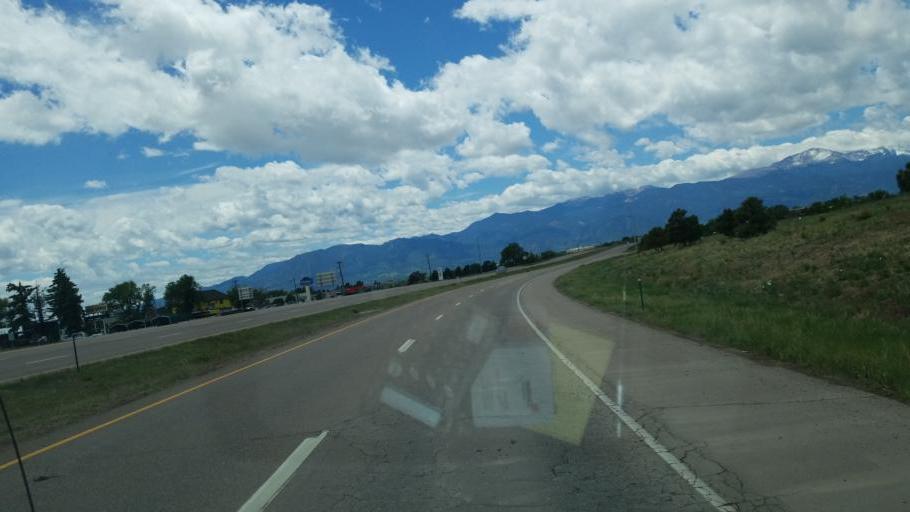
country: US
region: Colorado
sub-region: El Paso County
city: Cimarron Hills
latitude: 38.8405
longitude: -104.6959
